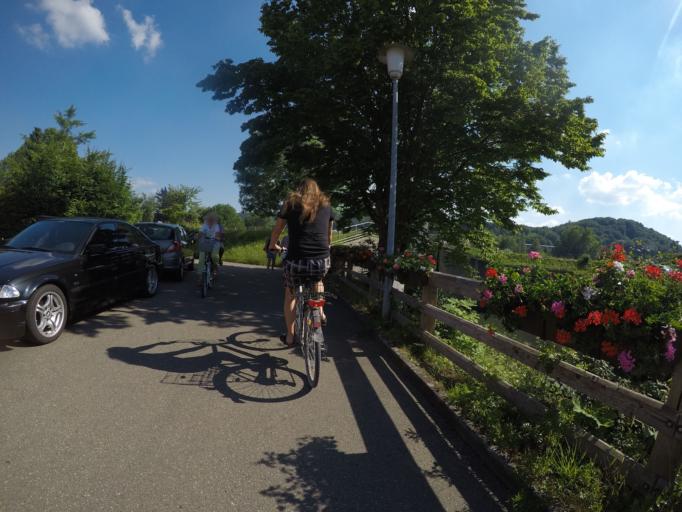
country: DE
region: Bavaria
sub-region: Lower Bavaria
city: Ihrlerstein
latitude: 48.9168
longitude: 11.8676
